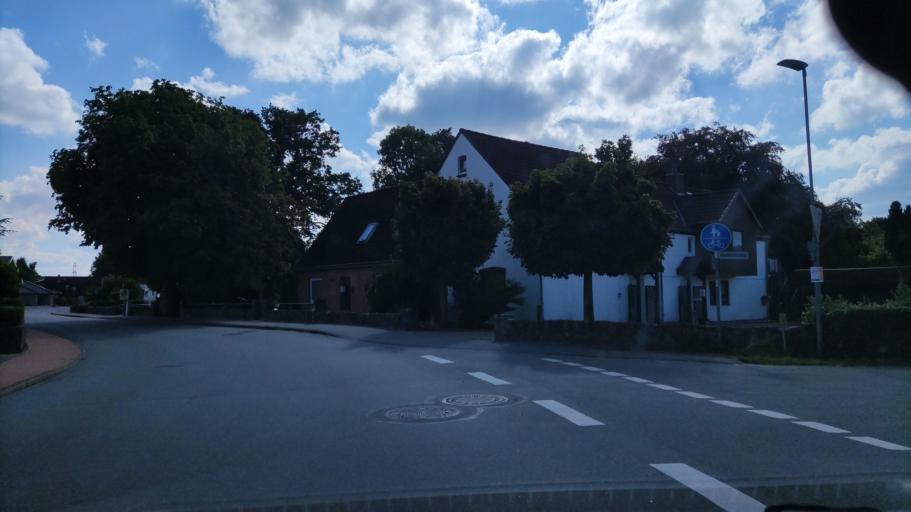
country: DE
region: Schleswig-Holstein
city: Alt Duvenstedt
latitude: 54.3626
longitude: 9.6463
